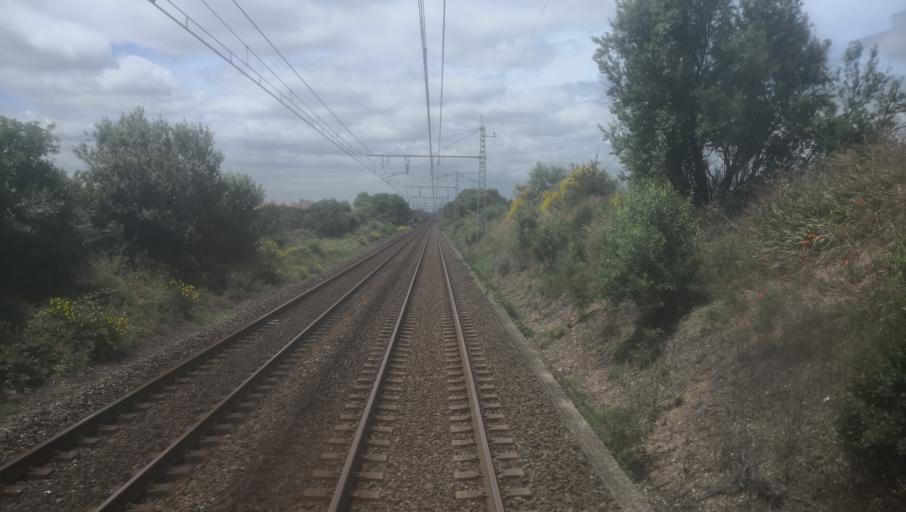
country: FR
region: Languedoc-Roussillon
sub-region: Departement de l'Aude
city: Carcassonne
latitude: 43.2195
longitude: 2.3759
